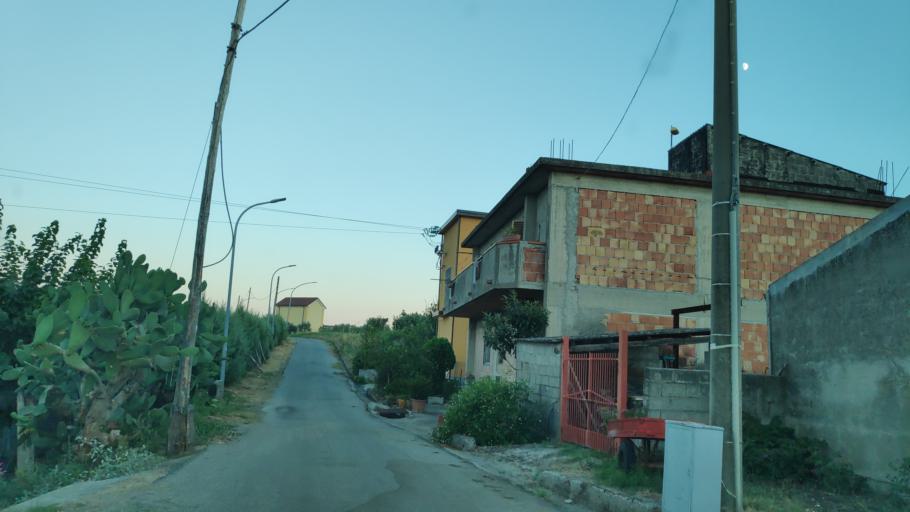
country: IT
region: Calabria
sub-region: Provincia di Reggio Calabria
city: Riace Marina
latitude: 38.3983
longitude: 16.5208
